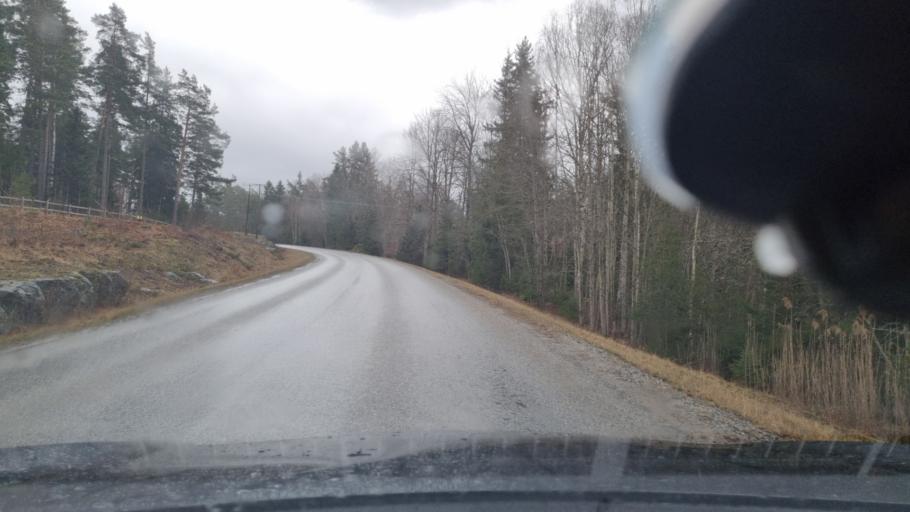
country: SE
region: Stockholm
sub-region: Sigtuna Kommun
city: Sigtuna
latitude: 59.5614
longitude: 17.7116
